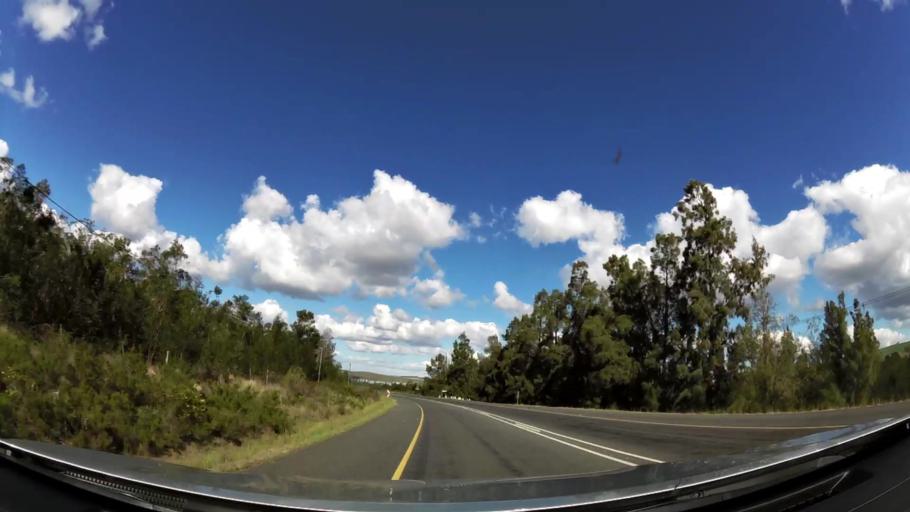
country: ZA
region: Western Cape
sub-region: Overberg District Municipality
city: Swellendam
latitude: -34.0308
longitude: 20.4203
